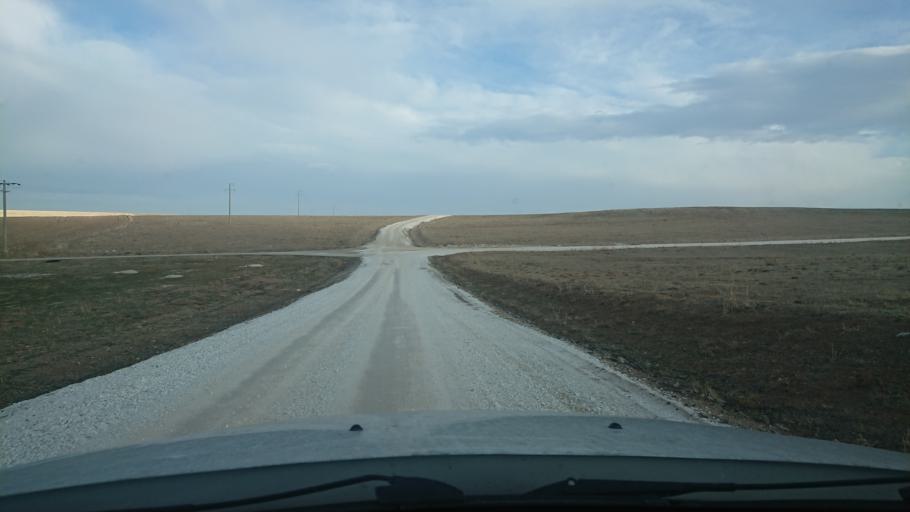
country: TR
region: Aksaray
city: Agacoren
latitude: 38.7372
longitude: 33.8696
